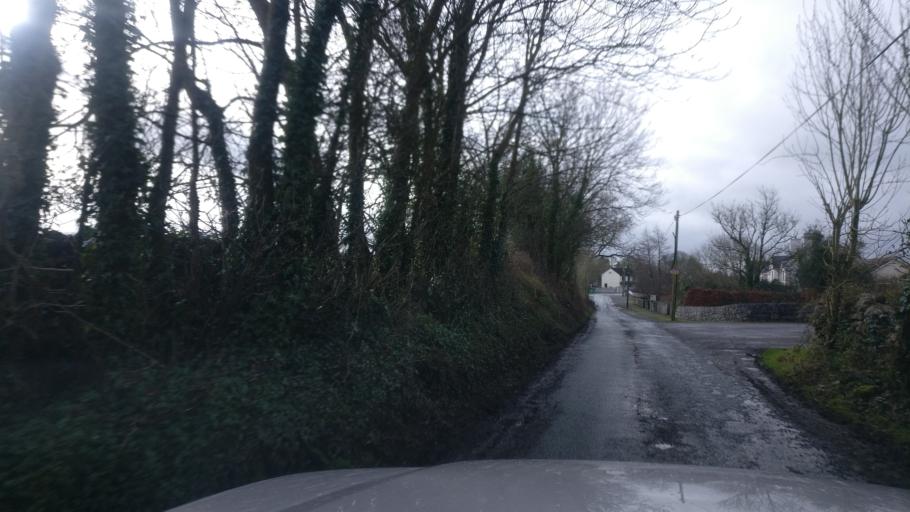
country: IE
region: Connaught
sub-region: County Galway
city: Athenry
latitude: 53.2647
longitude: -8.7929
